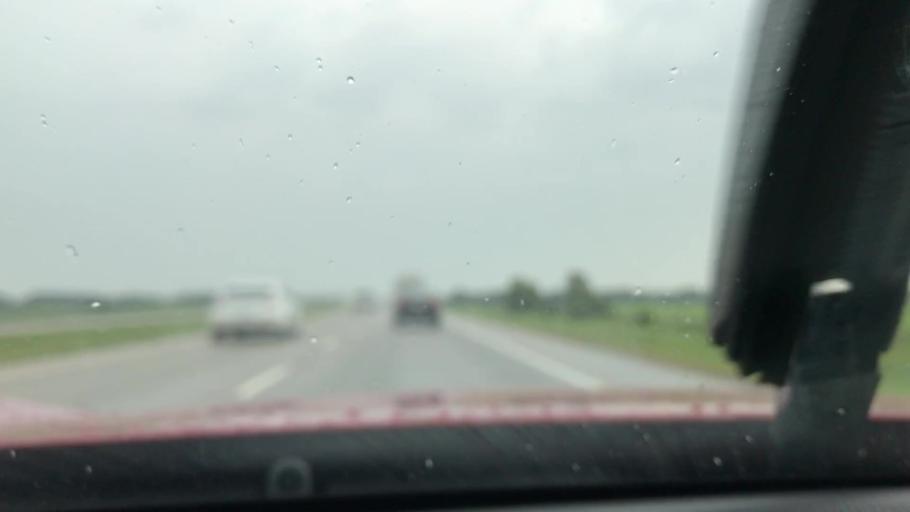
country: CA
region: Alberta
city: Ponoka
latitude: 52.8218
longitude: -113.6442
